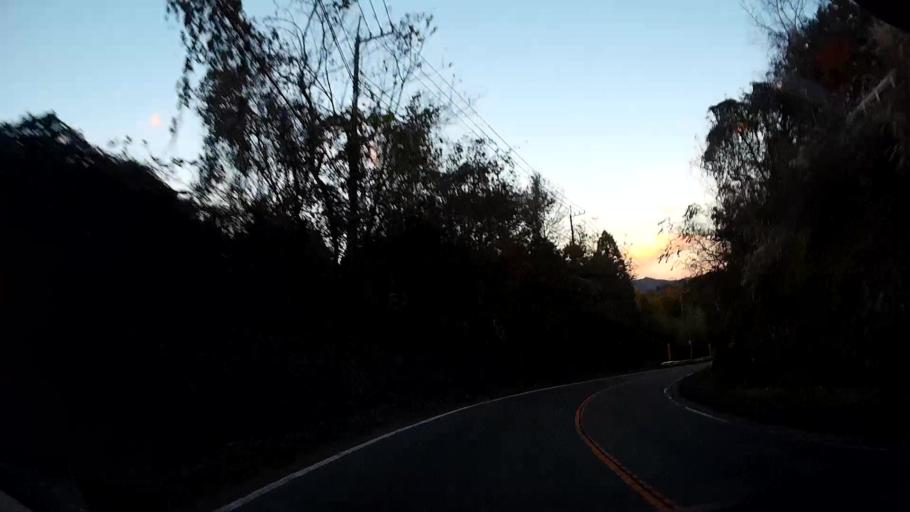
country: JP
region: Yamanashi
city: Uenohara
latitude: 35.5770
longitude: 139.2246
